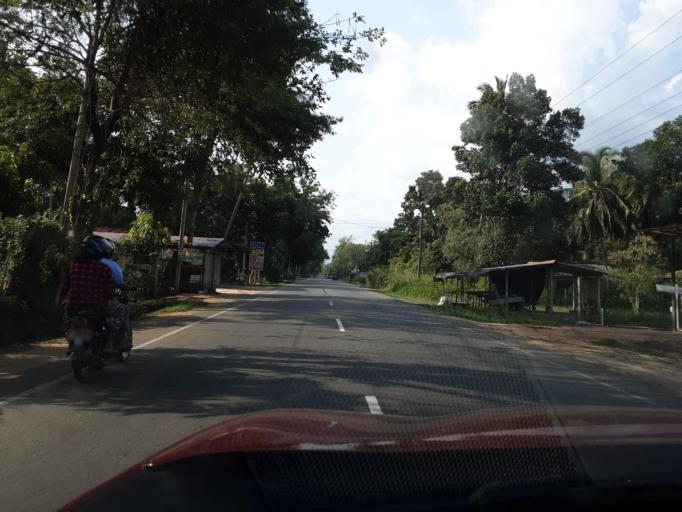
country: LK
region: Uva
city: Haputale
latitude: 6.6628
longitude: 81.1142
